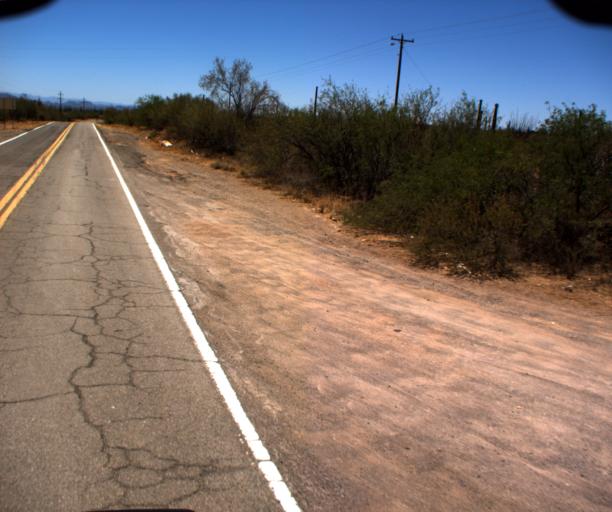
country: US
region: Arizona
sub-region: Pima County
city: Sells
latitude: 32.1587
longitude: -112.1105
